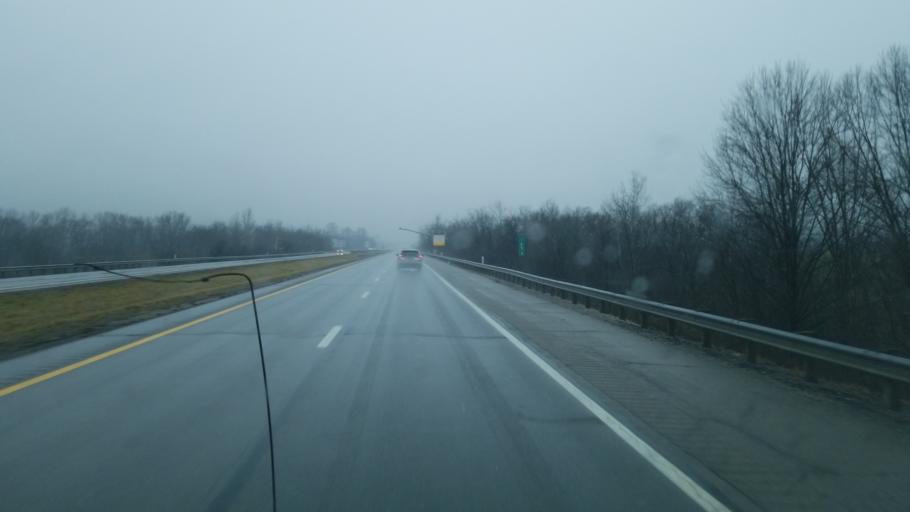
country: US
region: West Virginia
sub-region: Wood County
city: Mineral Wells
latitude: 39.1840
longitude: -81.5323
